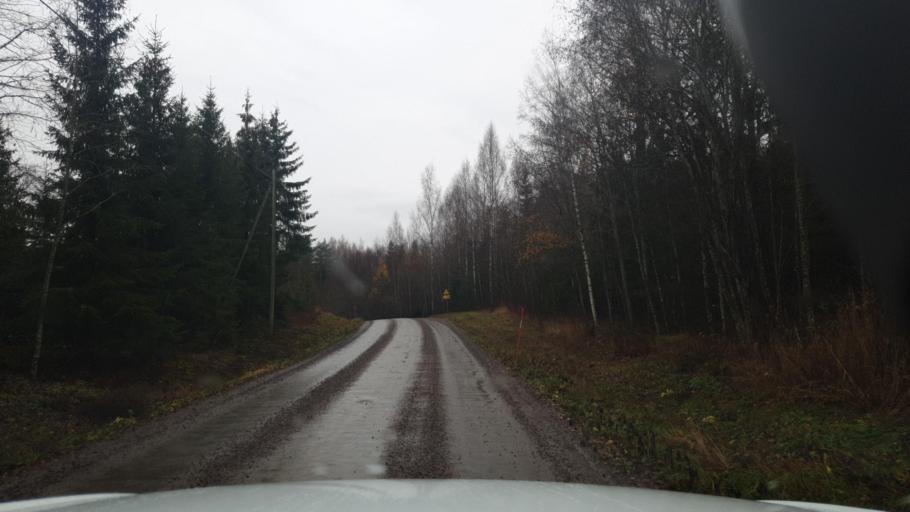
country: SE
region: Vaermland
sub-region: Eda Kommun
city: Amotfors
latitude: 59.7896
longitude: 12.3755
